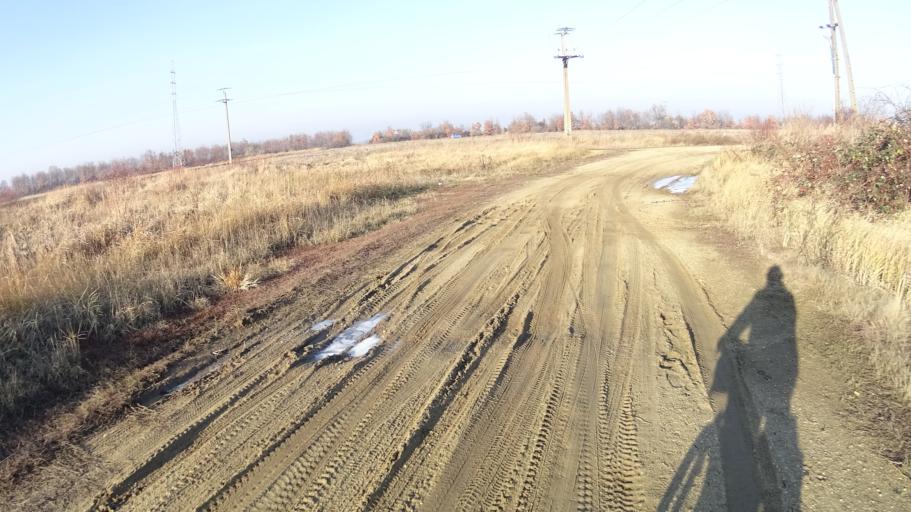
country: HU
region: Borsod-Abauj-Zemplen
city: Onod
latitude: 47.9950
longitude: 20.8791
